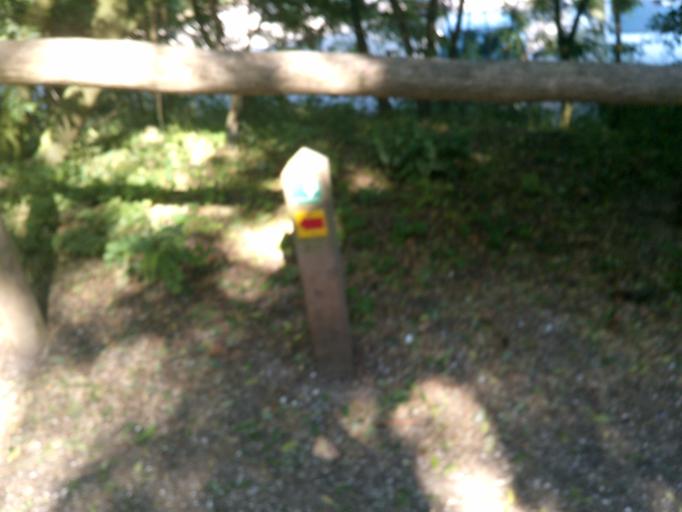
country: NL
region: South Holland
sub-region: Gemeente Noordwijkerhout
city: Noordwijkerhout
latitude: 52.2722
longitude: 4.4683
